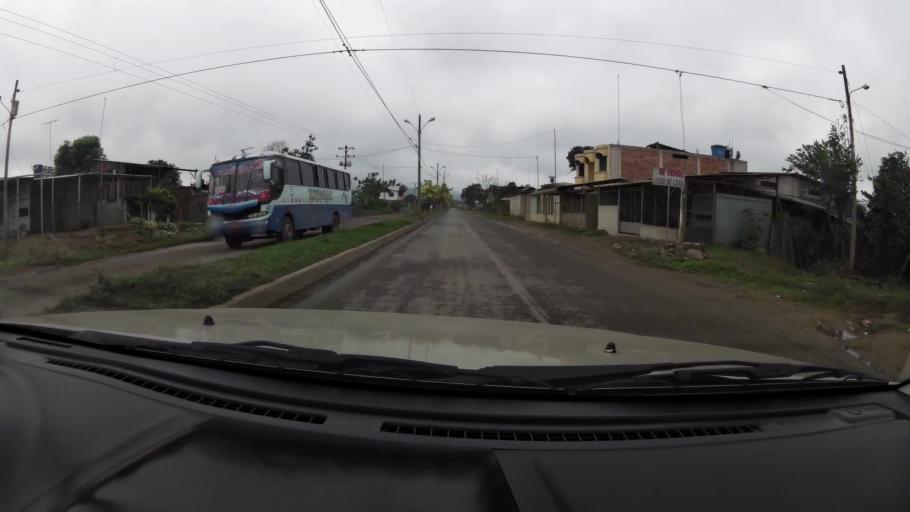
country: EC
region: El Oro
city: Pasaje
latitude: -3.3416
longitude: -79.8066
